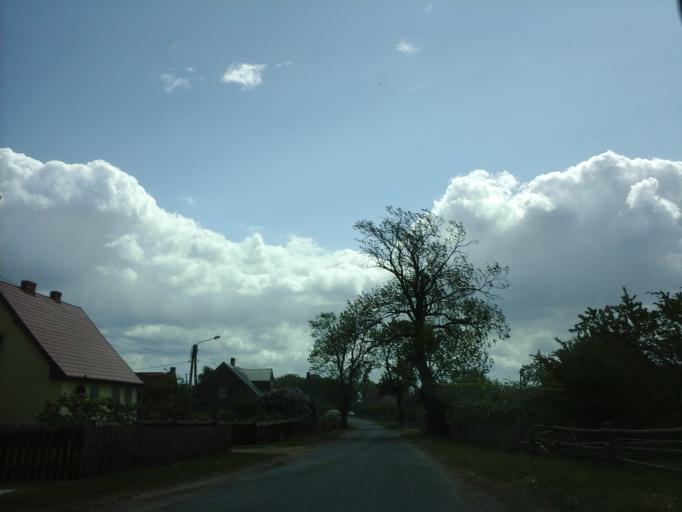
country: PL
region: West Pomeranian Voivodeship
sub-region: Powiat choszczenski
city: Choszczno
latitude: 53.1109
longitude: 15.4037
